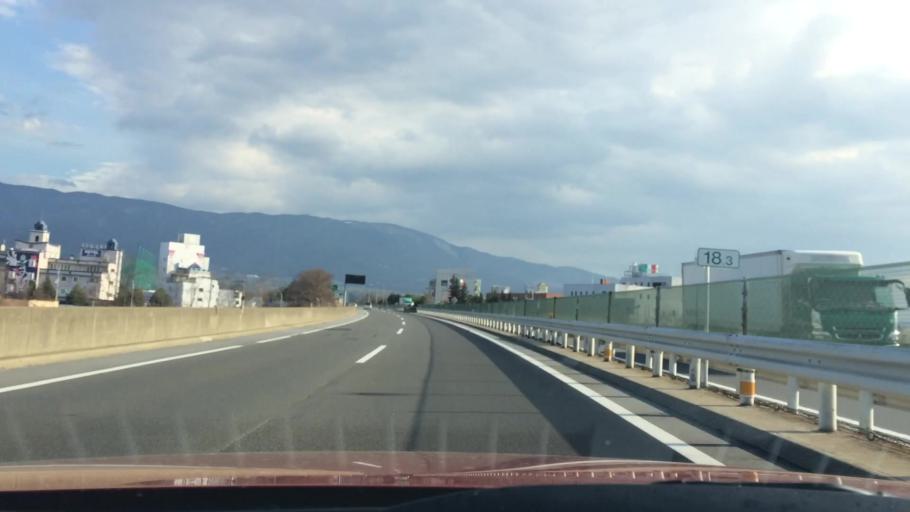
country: JP
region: Nagano
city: Matsumoto
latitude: 36.1719
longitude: 137.9455
